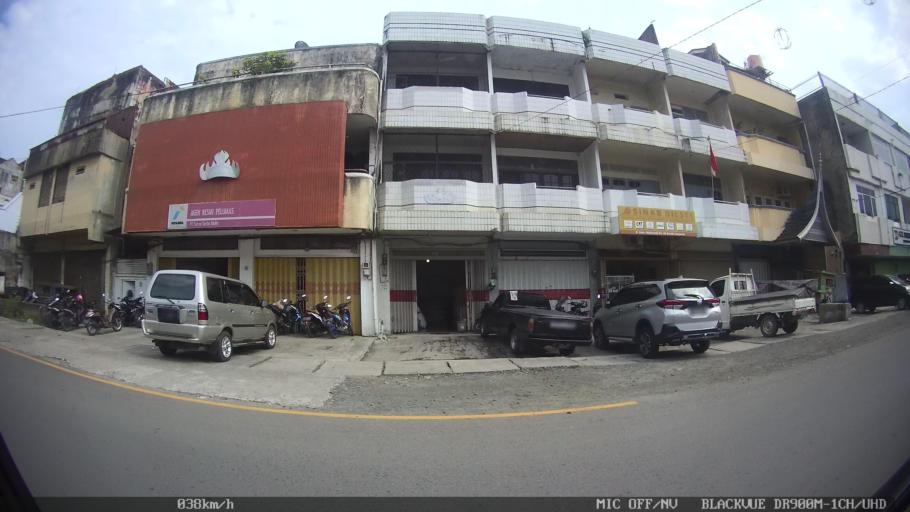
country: ID
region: Lampung
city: Bandarlampung
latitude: -5.4470
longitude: 105.2706
